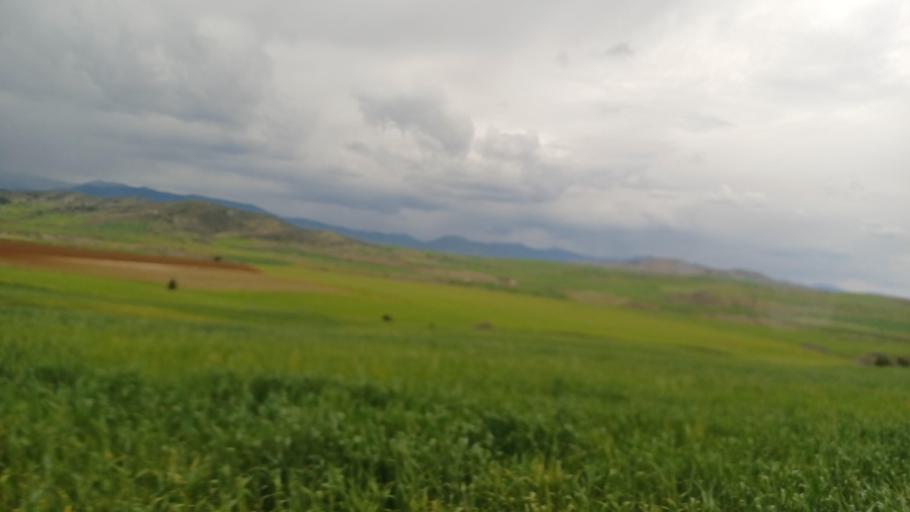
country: CY
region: Lefkosia
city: Astromeritis
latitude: 35.0953
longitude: 32.9514
